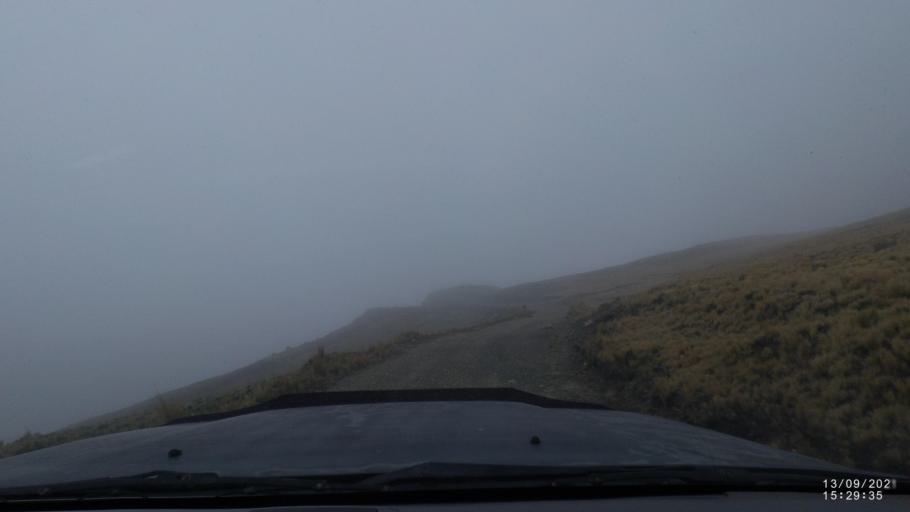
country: BO
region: Cochabamba
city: Colomi
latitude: -17.3457
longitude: -65.7580
